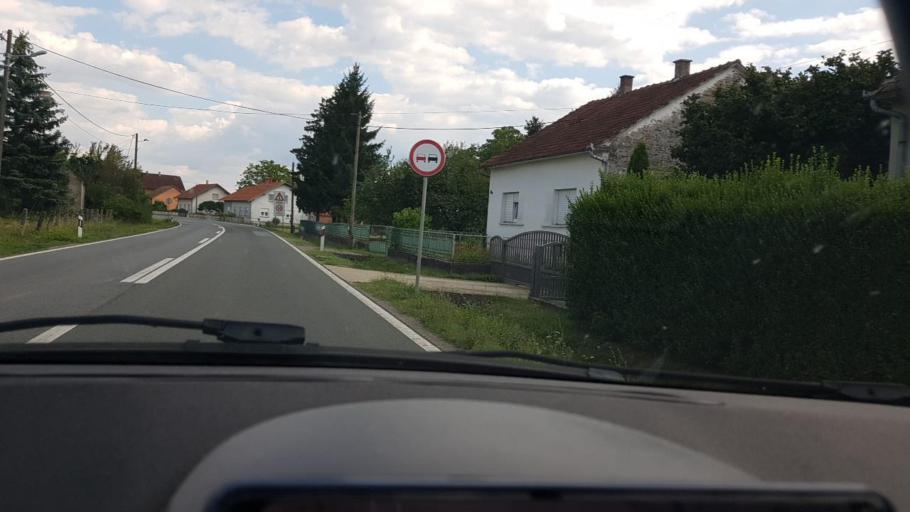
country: HR
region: Bjelovarsko-Bilogorska
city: Zdralovi
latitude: 45.8570
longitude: 16.9246
